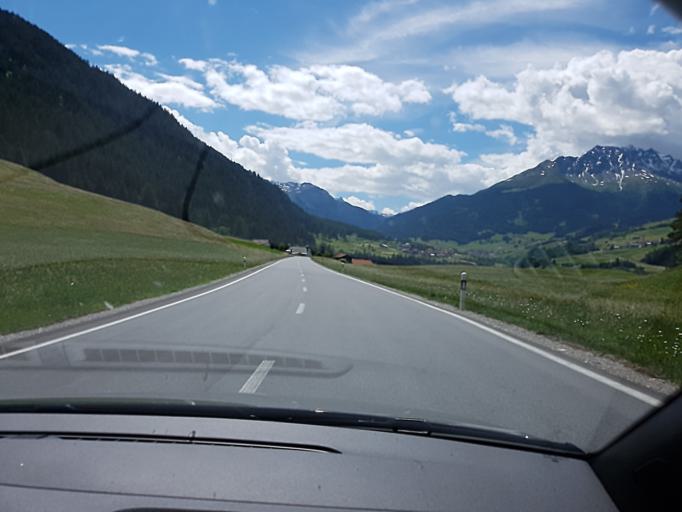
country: CH
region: Grisons
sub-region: Albula District
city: Tiefencastel
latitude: 46.6280
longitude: 9.5841
